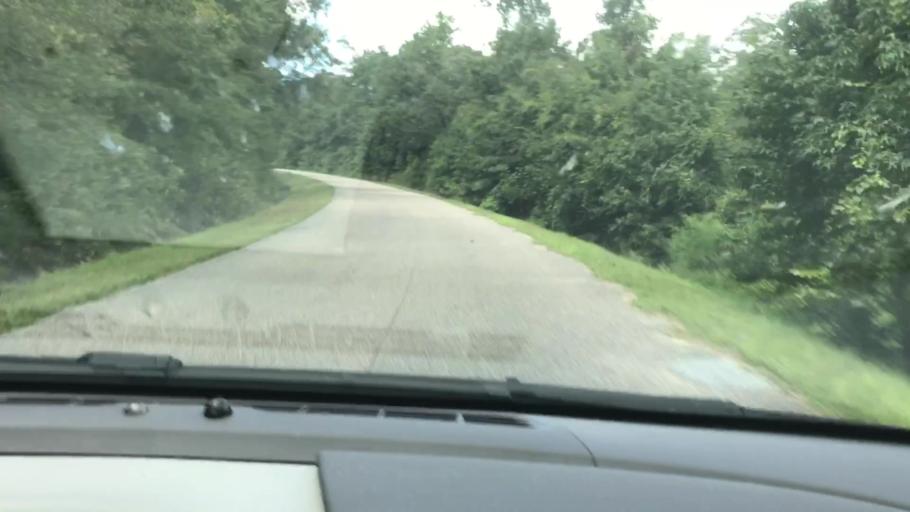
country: US
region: Georgia
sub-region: Clay County
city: Fort Gaines
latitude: 31.7400
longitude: -85.0749
